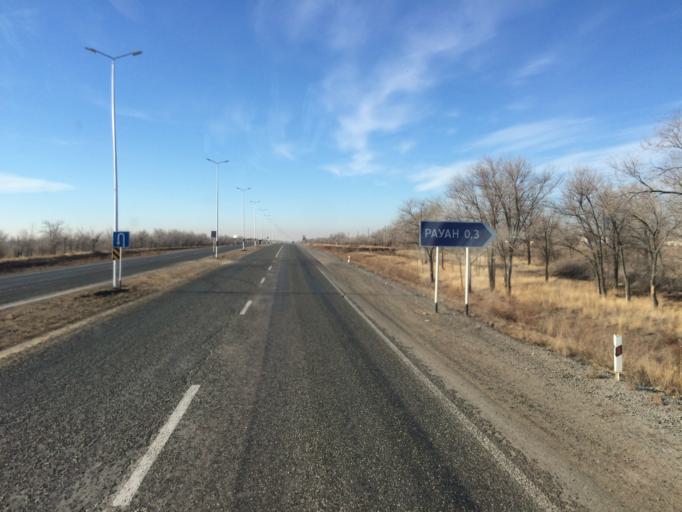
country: KZ
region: Aqtoebe
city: Aqtobe
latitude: 50.2914
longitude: 57.3589
